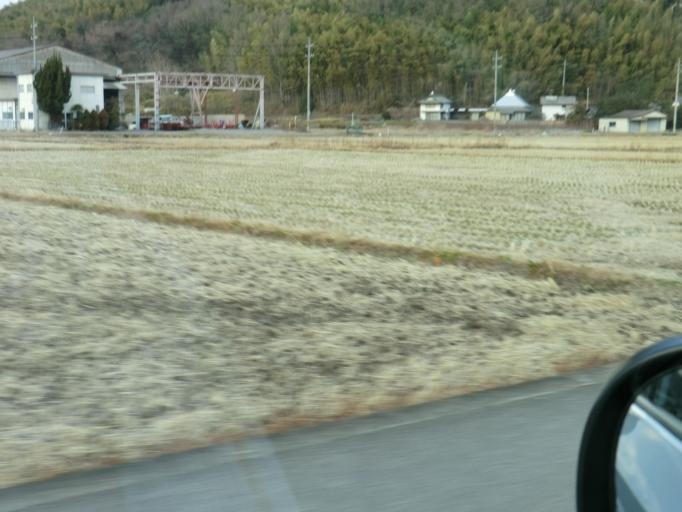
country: JP
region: Okayama
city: Okayama-shi
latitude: 34.7297
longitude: 134.0211
